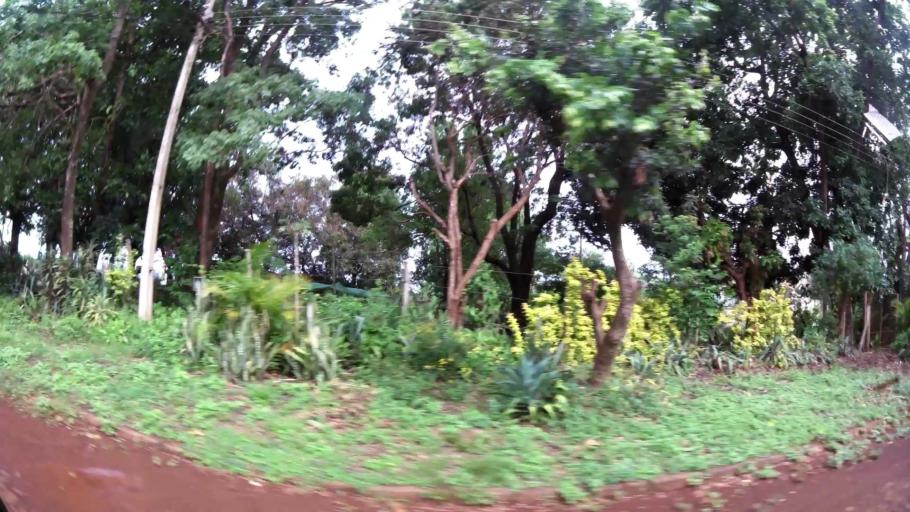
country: PY
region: Alto Parana
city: Ciudad del Este
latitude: -25.3929
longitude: -54.6375
